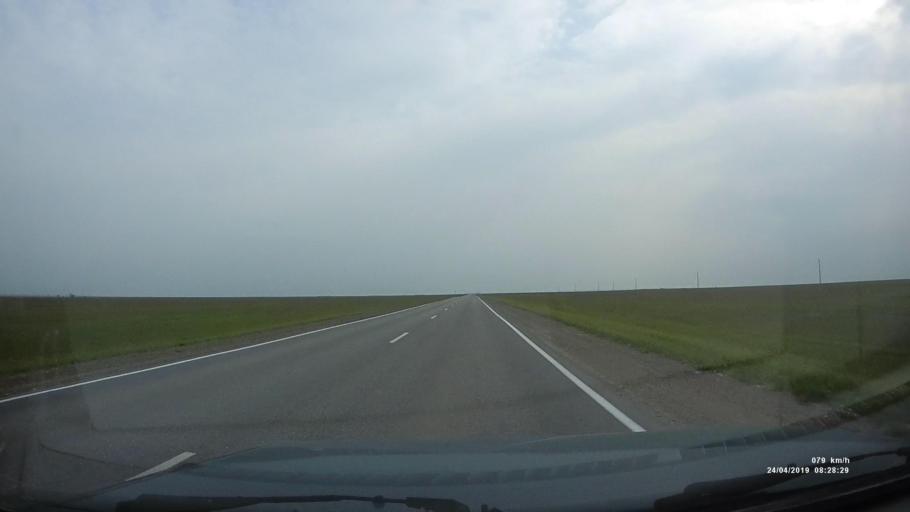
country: RU
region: Kalmykiya
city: Priyutnoye
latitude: 46.1448
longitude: 43.8164
